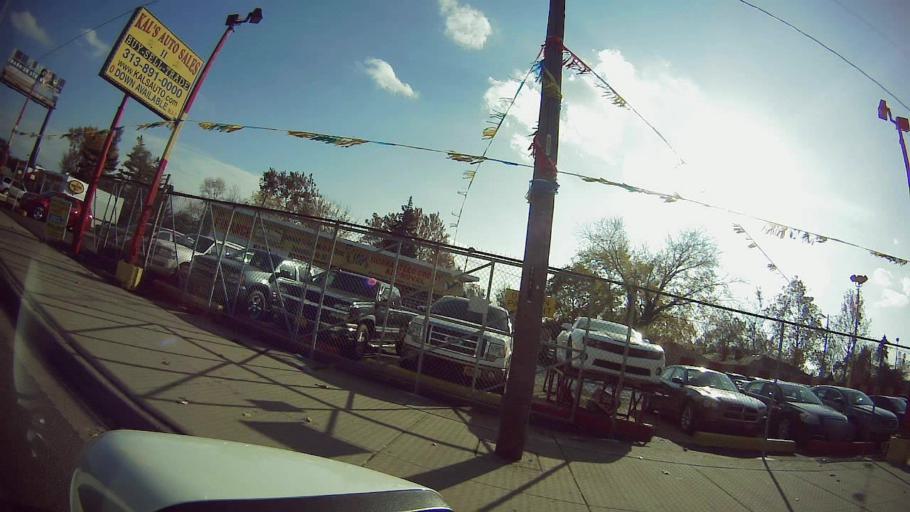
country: US
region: Michigan
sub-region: Macomb County
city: Warren
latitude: 42.4475
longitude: -83.0523
